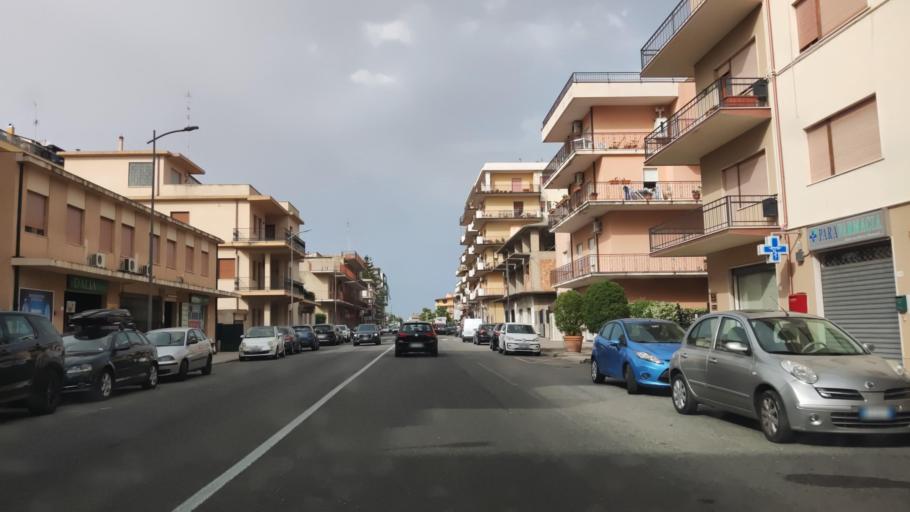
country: IT
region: Calabria
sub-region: Provincia di Reggio Calabria
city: Locri
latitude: 38.2401
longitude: 16.2702
